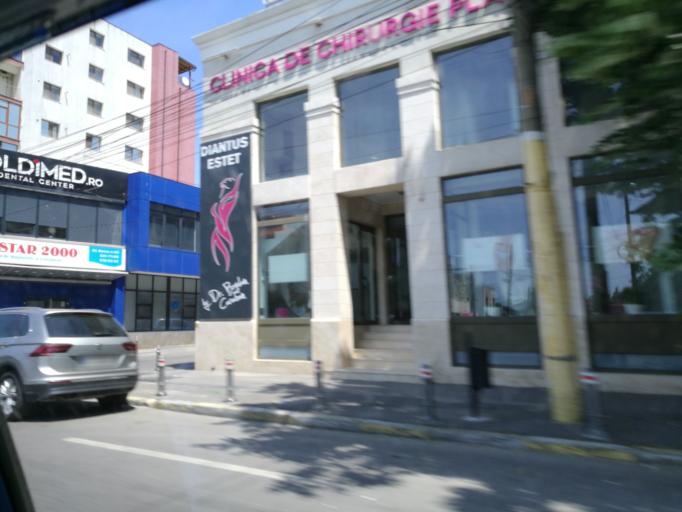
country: RO
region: Constanta
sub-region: Municipiul Constanta
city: Constanta
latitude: 44.2026
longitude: 28.6456
